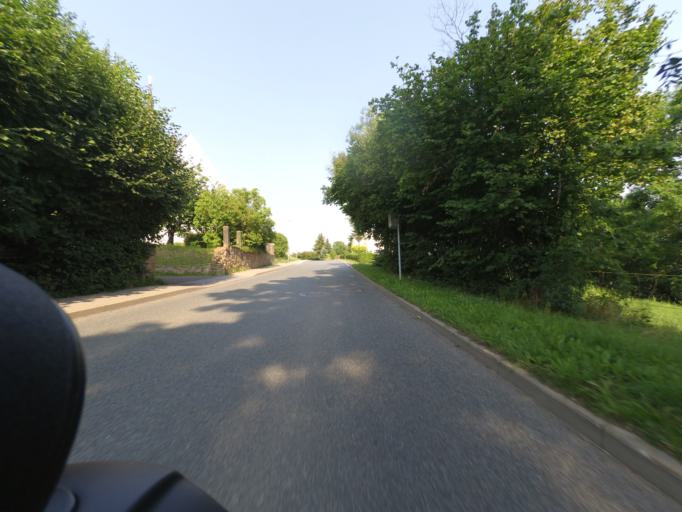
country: DE
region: Saxony
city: Rosswein
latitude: 51.0502
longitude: 13.1788
